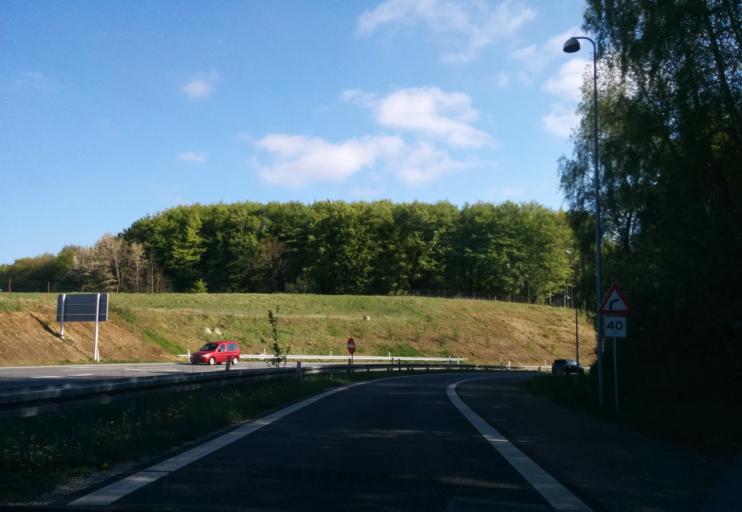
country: DK
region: South Denmark
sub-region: Vejle Kommune
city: Vejle
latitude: 55.7243
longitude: 9.5783
